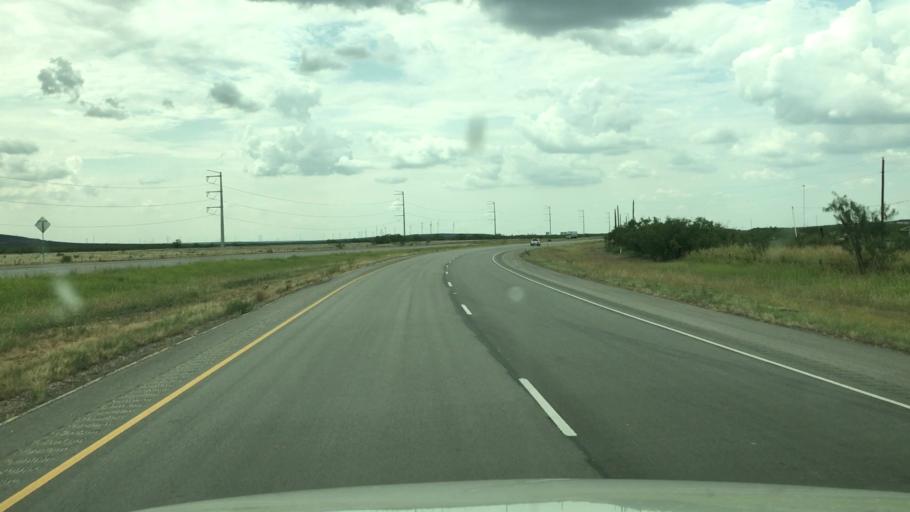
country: US
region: Texas
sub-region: Glasscock County
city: Garden City
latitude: 31.9684
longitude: -101.2379
